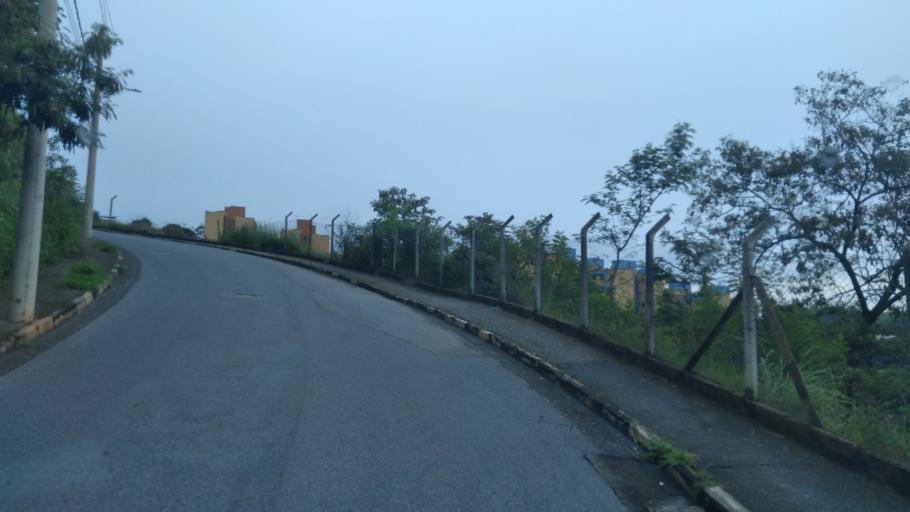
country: BR
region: Minas Gerais
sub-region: Belo Horizonte
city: Belo Horizonte
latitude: -19.9107
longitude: -43.8827
